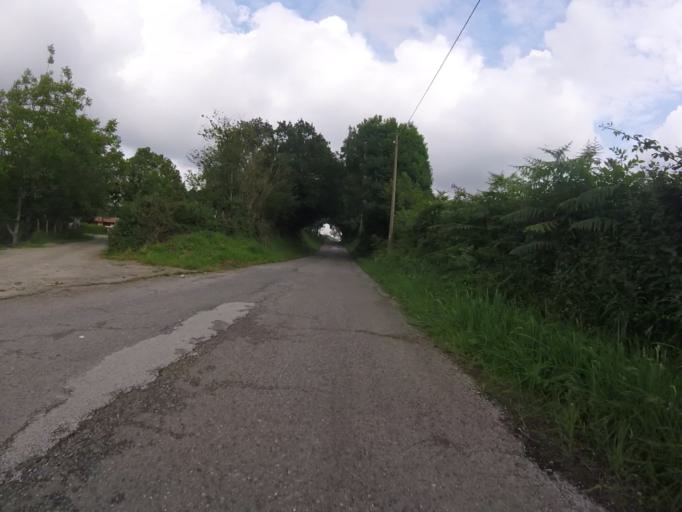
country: ES
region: Basque Country
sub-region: Provincia de Guipuzcoa
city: Pasaia
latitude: 43.3036
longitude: -1.9348
